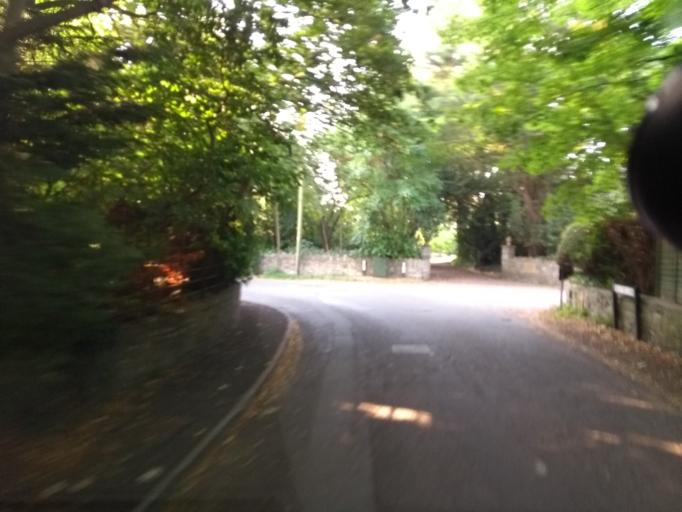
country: GB
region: England
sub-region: Somerset
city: Curry Rivel
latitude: 51.0189
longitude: -2.8523
